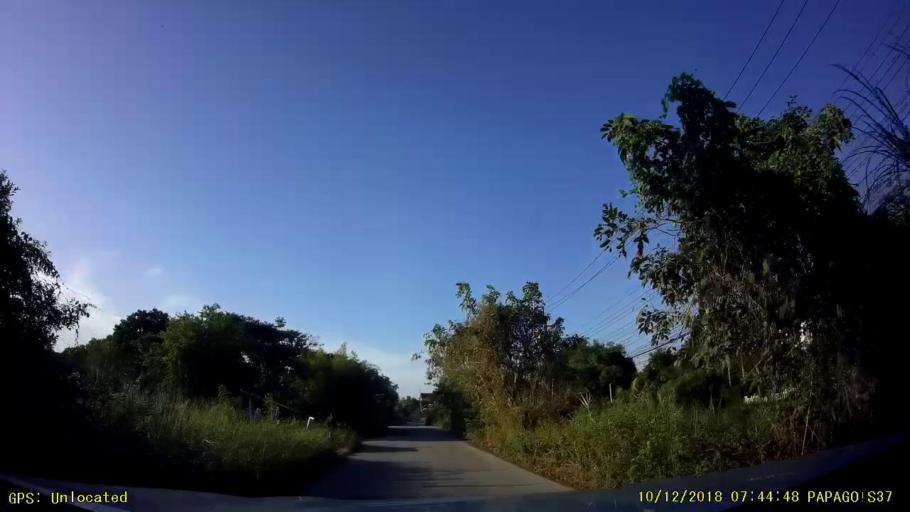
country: TH
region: Bangkok
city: Lat Krabang
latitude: 13.7869
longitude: 100.8247
